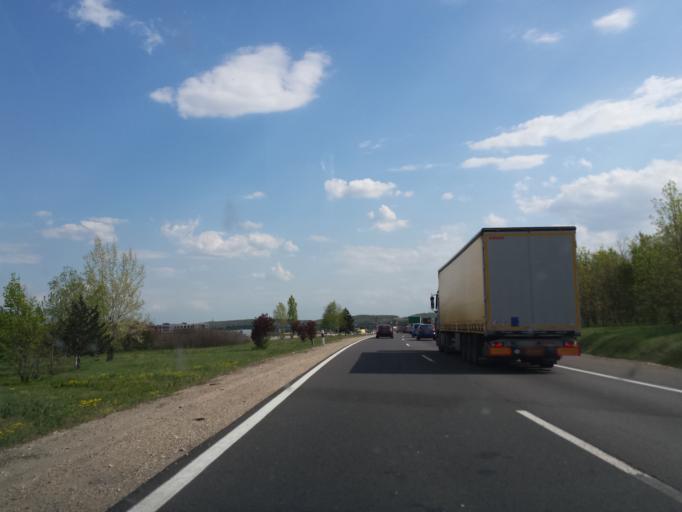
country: HU
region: Pest
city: Toeroekbalint
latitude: 47.4618
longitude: 18.8771
